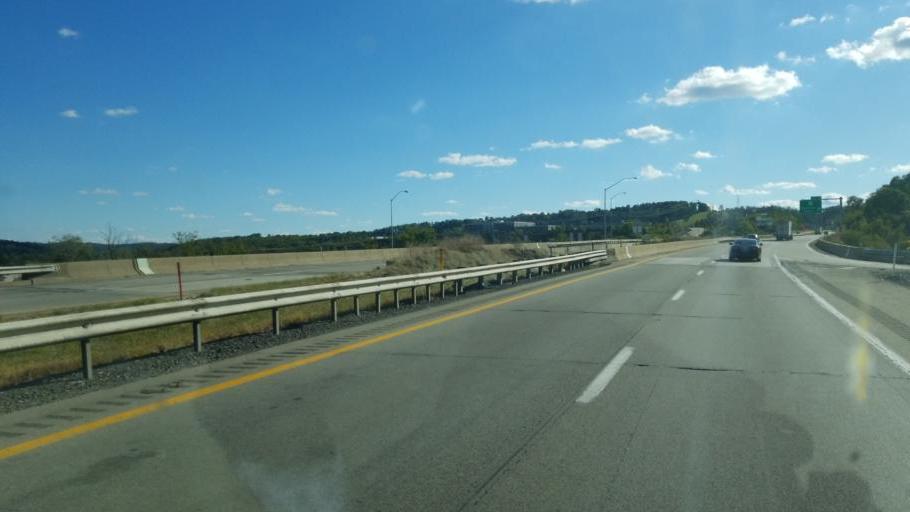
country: US
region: Pennsylvania
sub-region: Washington County
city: Wolfdale
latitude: 40.1628
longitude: -80.2778
